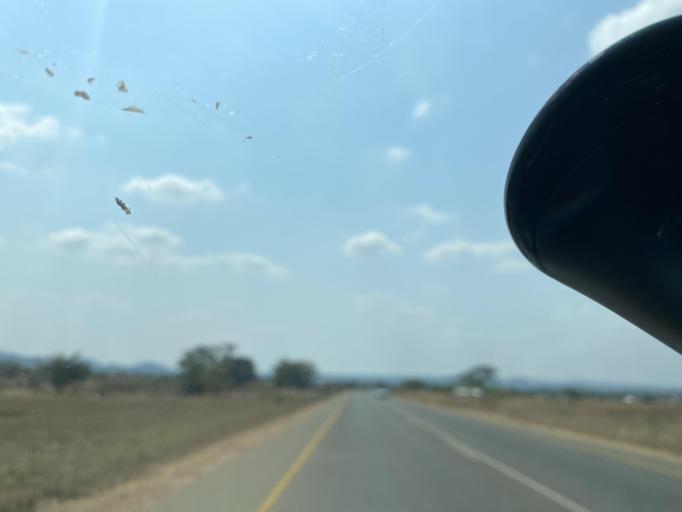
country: ZM
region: Lusaka
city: Chongwe
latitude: -15.5743
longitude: 28.6989
